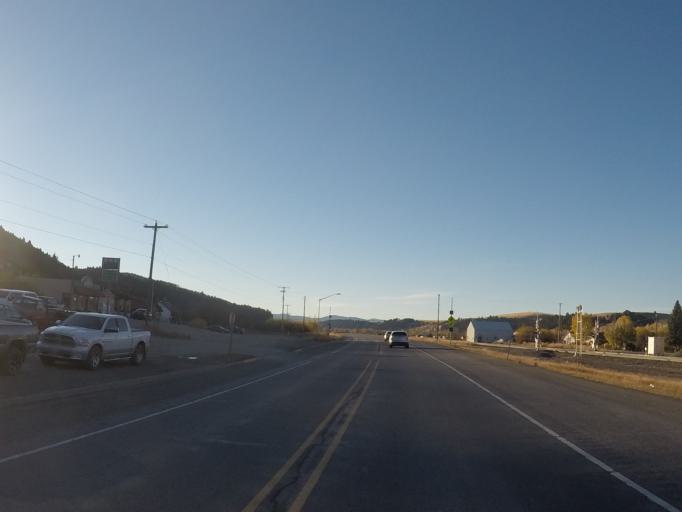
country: US
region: Montana
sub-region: Lewis and Clark County
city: Helena West Side
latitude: 46.5608
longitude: -112.4291
